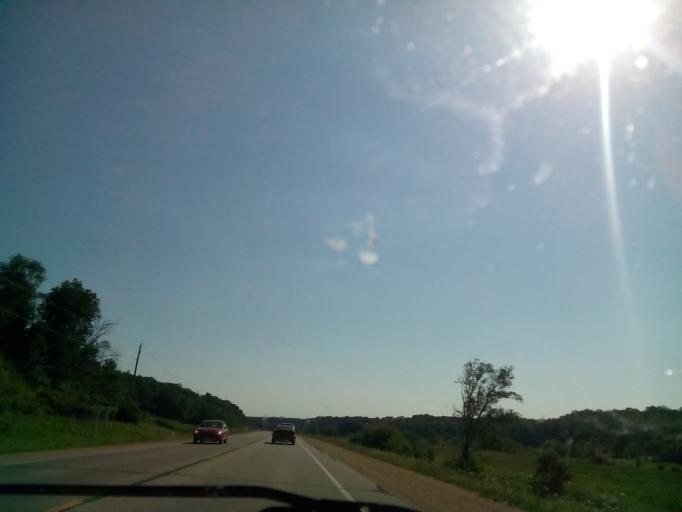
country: US
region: Wisconsin
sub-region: Green County
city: New Glarus
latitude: 42.8556
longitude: -89.6219
